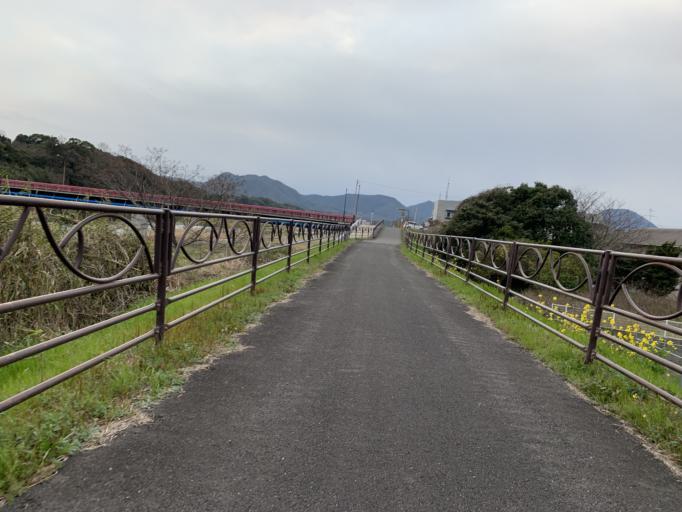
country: JP
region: Oita
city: Bungo-Takada-shi
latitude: 33.5348
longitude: 131.3518
